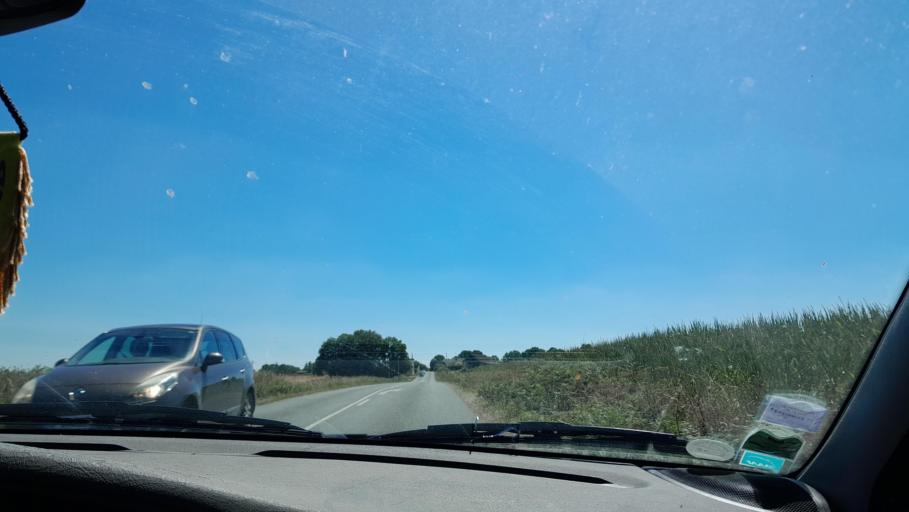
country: FR
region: Pays de la Loire
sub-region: Departement de la Mayenne
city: Congrier
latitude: 47.8714
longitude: -1.1298
